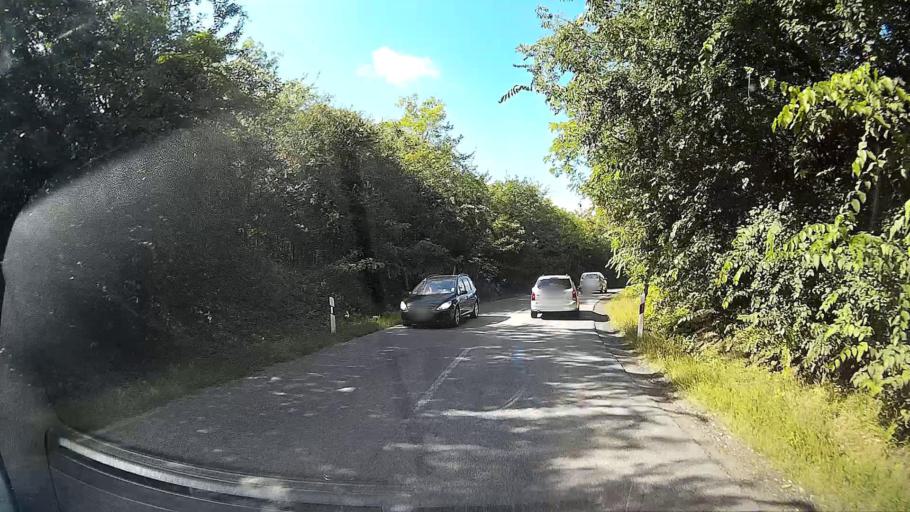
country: HU
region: Pest
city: Mogyorod
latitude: 47.5839
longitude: 19.2326
